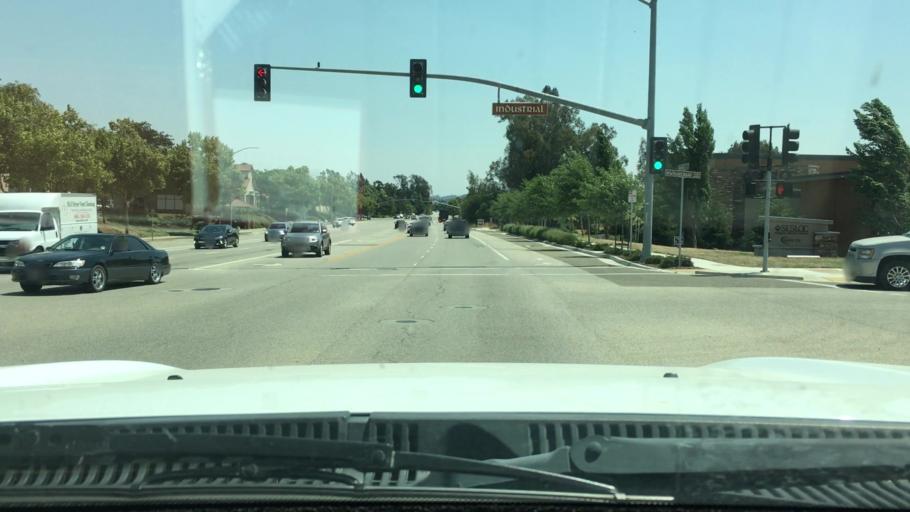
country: US
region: California
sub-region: San Luis Obispo County
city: San Luis Obispo
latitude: 35.2512
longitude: -120.6447
